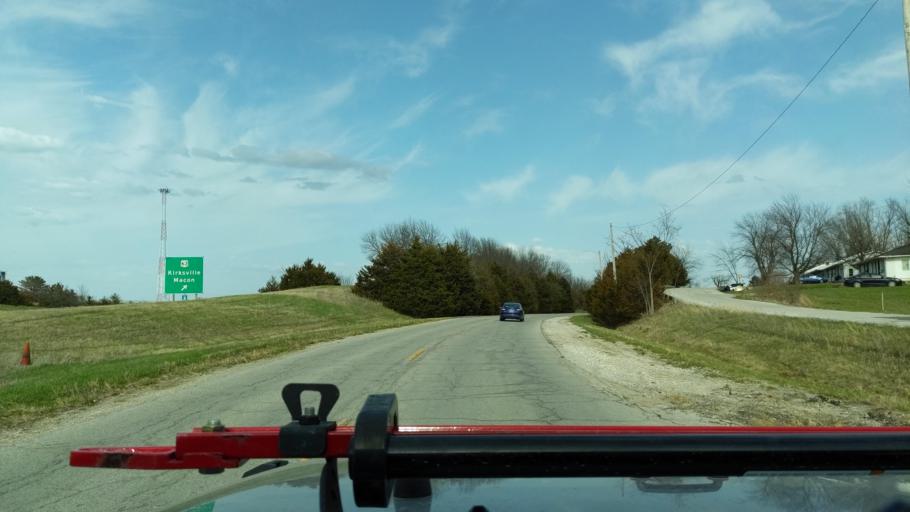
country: US
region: Missouri
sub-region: Macon County
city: Macon
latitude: 39.7518
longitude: -92.4734
